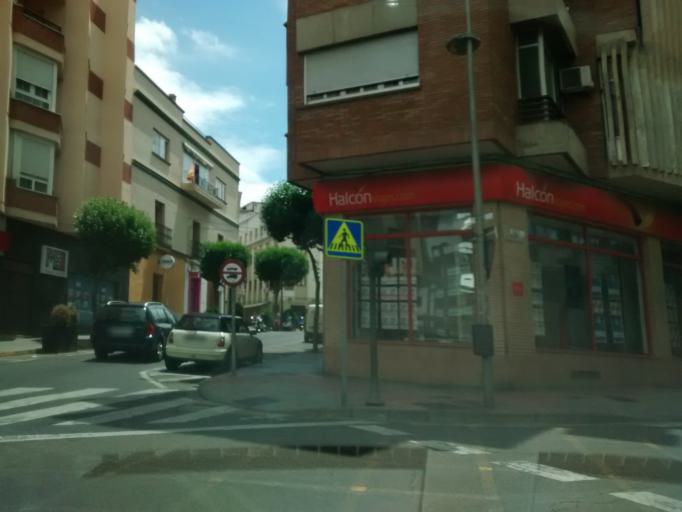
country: ES
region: Extremadura
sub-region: Provincia de Badajoz
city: Merida
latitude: 38.9201
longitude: -6.3434
